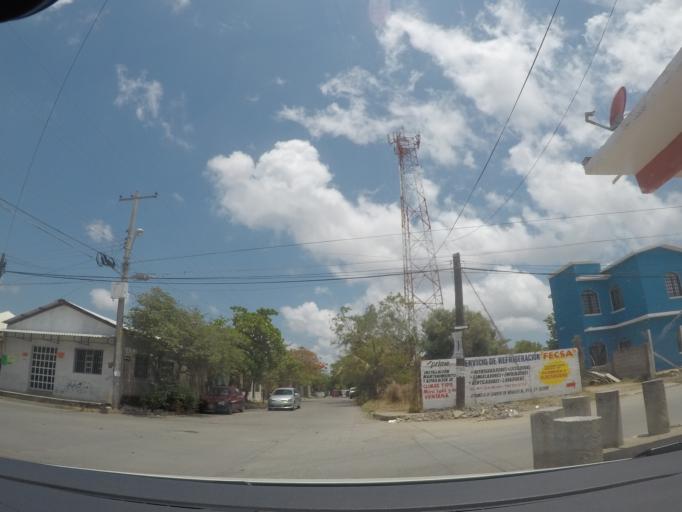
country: MX
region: Oaxaca
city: Juchitan de Zaragoza
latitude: 16.4384
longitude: -95.0132
